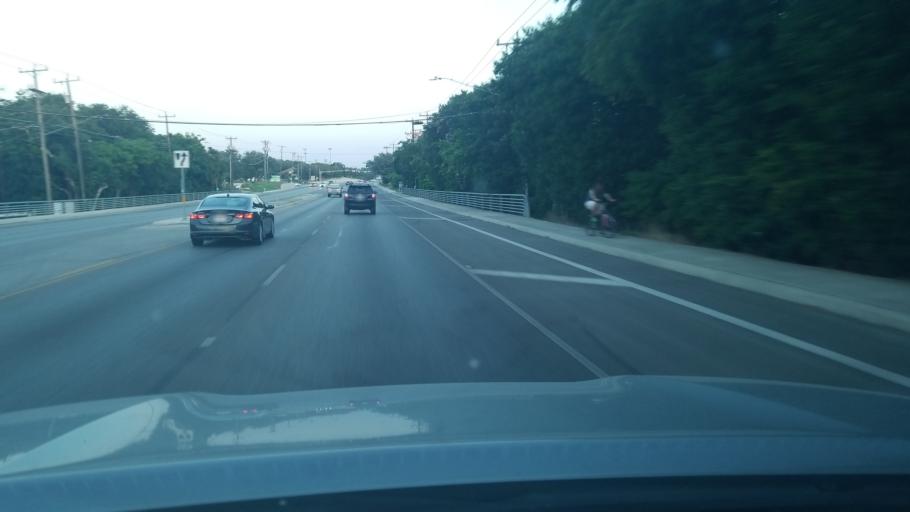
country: US
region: Texas
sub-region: Bexar County
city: Shavano Park
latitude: 29.5668
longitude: -98.5398
